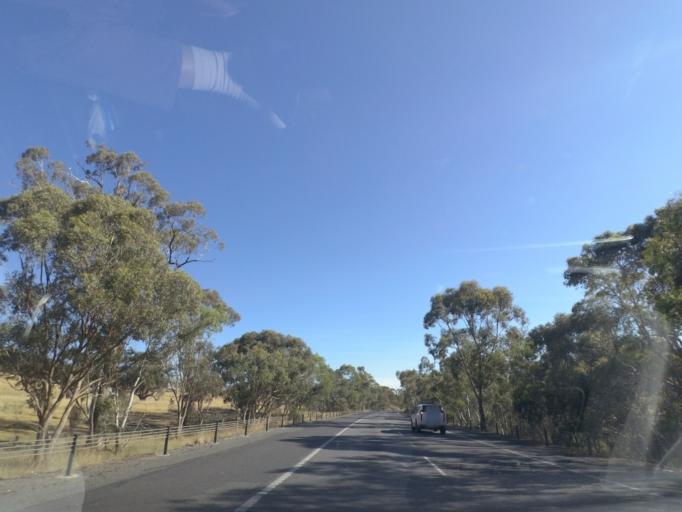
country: AU
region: Victoria
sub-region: Murrindindi
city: Kinglake West
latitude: -37.1661
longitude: 145.0779
